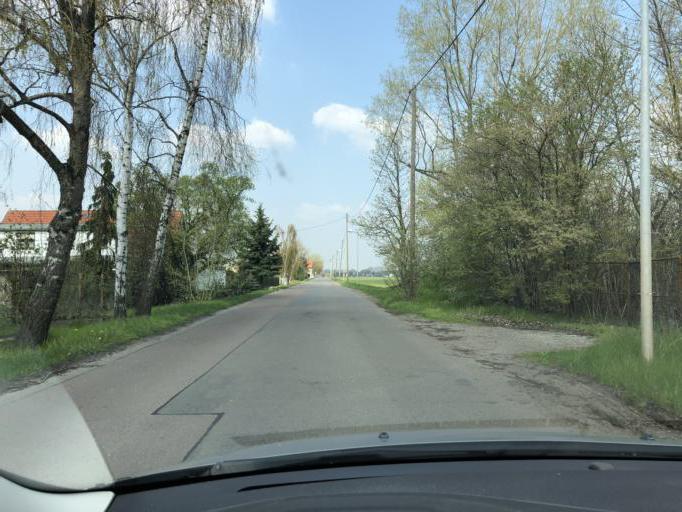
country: DE
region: Saxony-Anhalt
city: Landsberg
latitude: 51.5519
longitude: 12.1325
